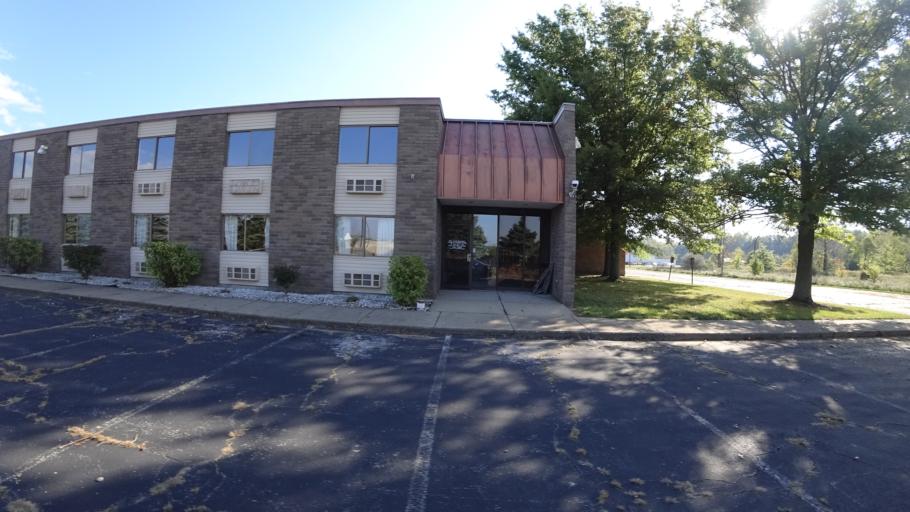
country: US
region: Michigan
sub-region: Saint Joseph County
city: Three Rivers
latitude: 41.9314
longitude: -85.6490
